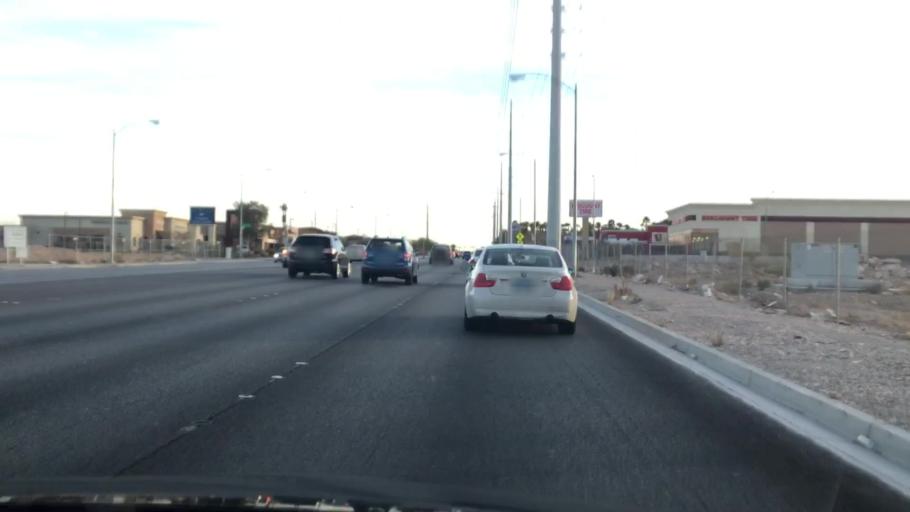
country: US
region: Nevada
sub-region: Clark County
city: Enterprise
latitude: 36.0621
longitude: -115.2795
